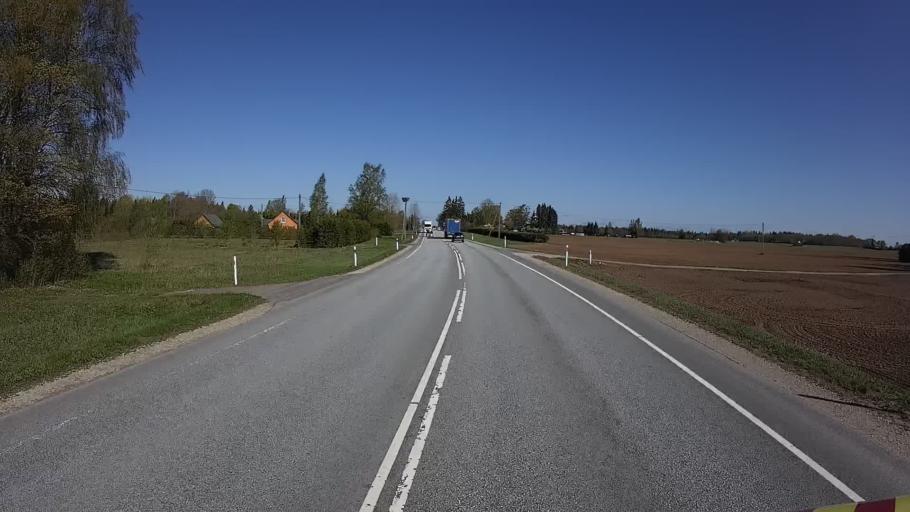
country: EE
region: Jaervamaa
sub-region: Paide linn
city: Paide
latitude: 58.8726
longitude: 25.7014
